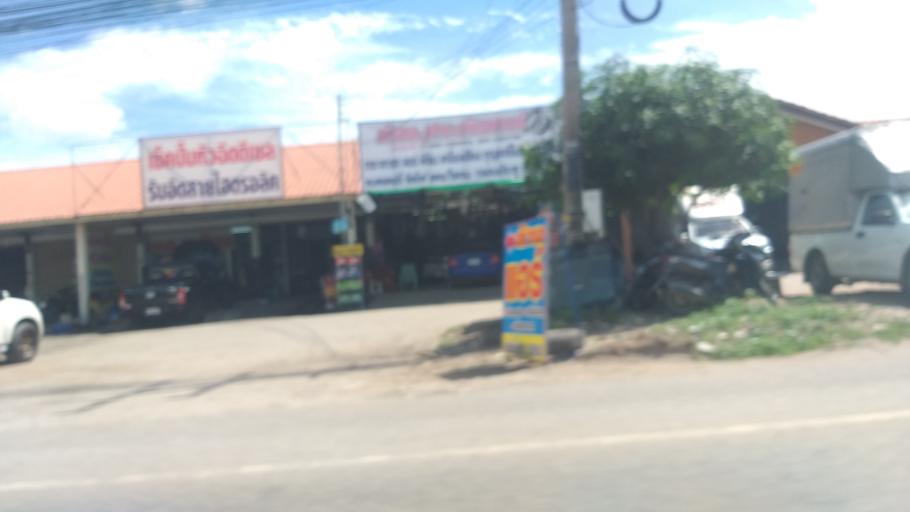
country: TH
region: Khon Kaen
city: Nong Ruea
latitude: 16.4899
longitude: 102.4499
